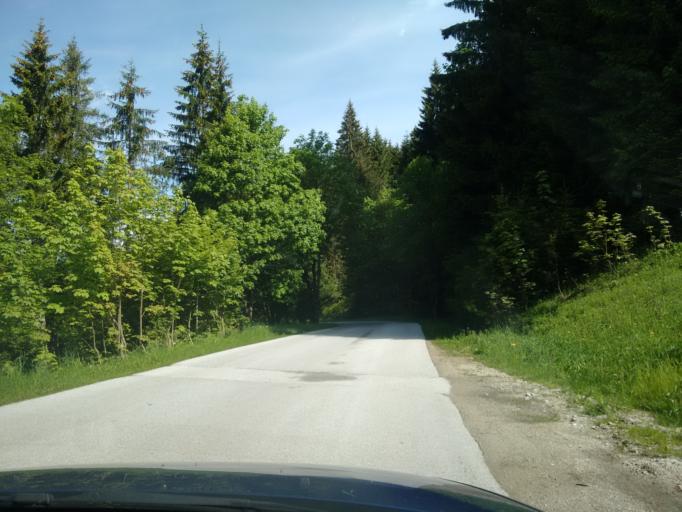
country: AT
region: Styria
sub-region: Politischer Bezirk Liezen
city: Altaussee
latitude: 47.6621
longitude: 13.7496
